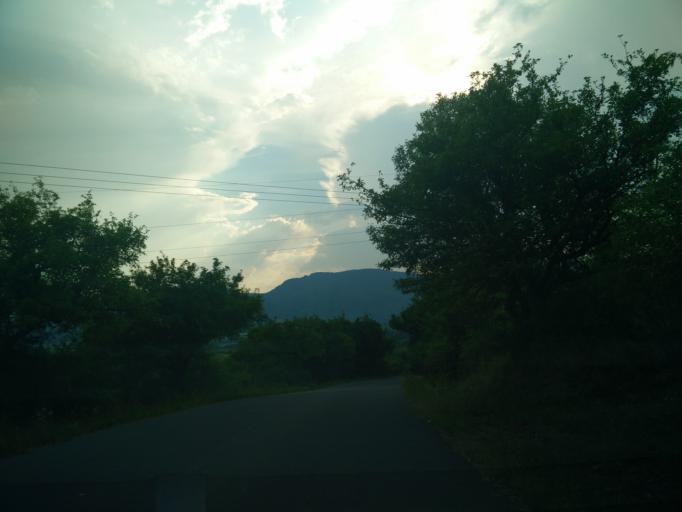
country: SK
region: Banskobystricky
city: Ziar nad Hronom
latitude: 48.6502
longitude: 18.7973
